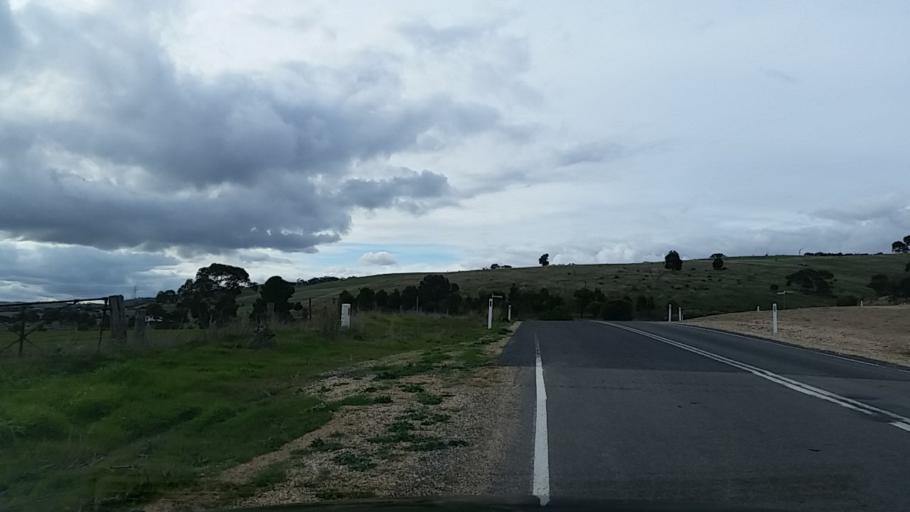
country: AU
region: South Australia
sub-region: Mount Barker
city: Callington
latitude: -35.0158
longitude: 139.0524
